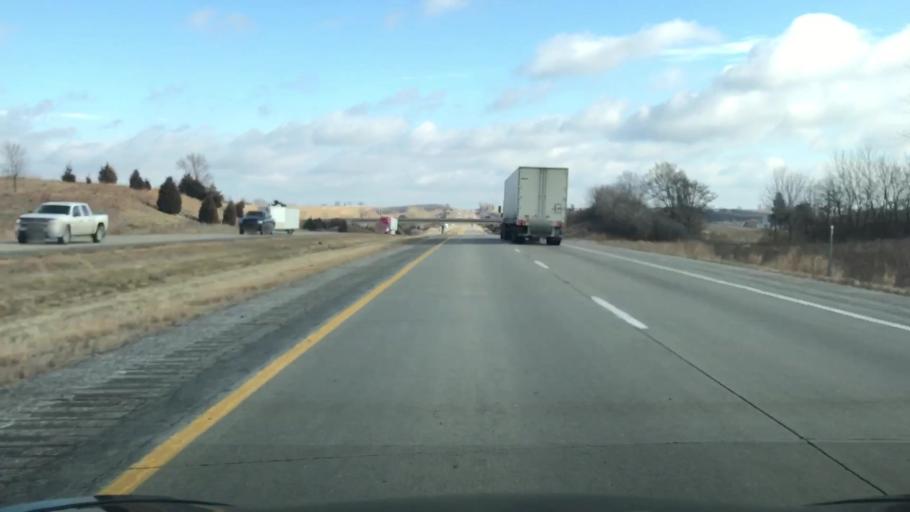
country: US
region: Iowa
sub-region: Cass County
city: Atlantic
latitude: 41.4971
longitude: -94.9154
